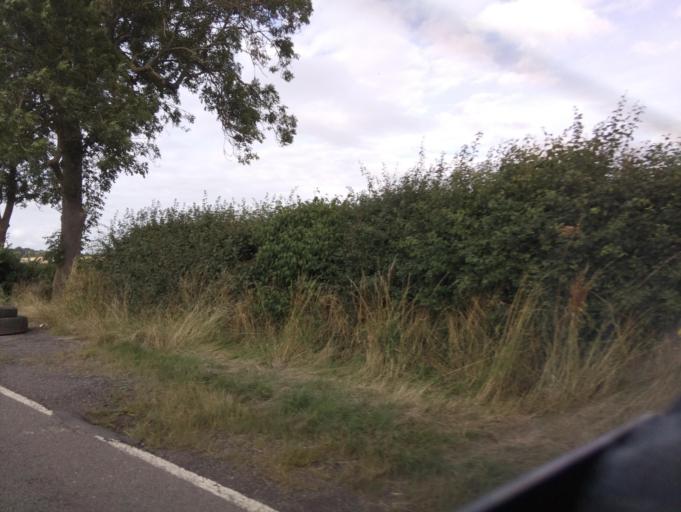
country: GB
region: England
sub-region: Warwickshire
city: Dunchurch
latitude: 52.3235
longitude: -1.3033
